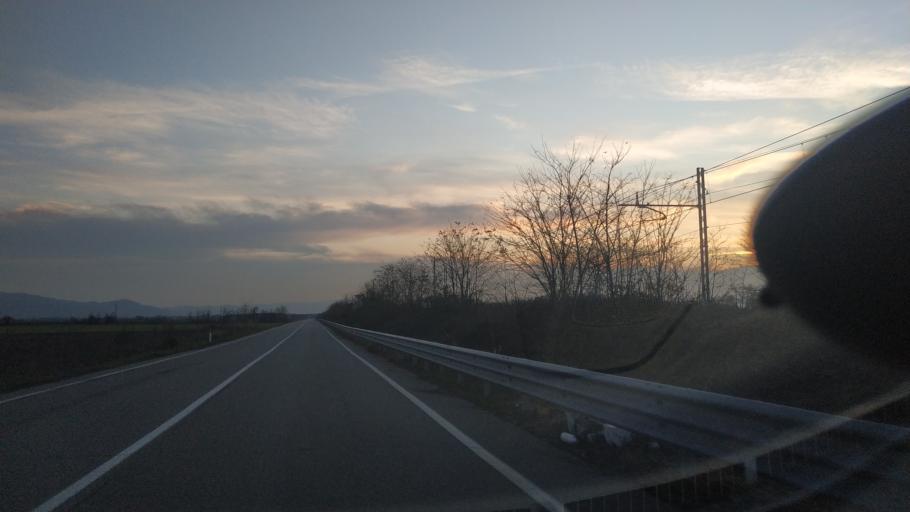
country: IT
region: Piedmont
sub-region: Provincia di Torino
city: Montanaro
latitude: 45.2548
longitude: 7.8669
